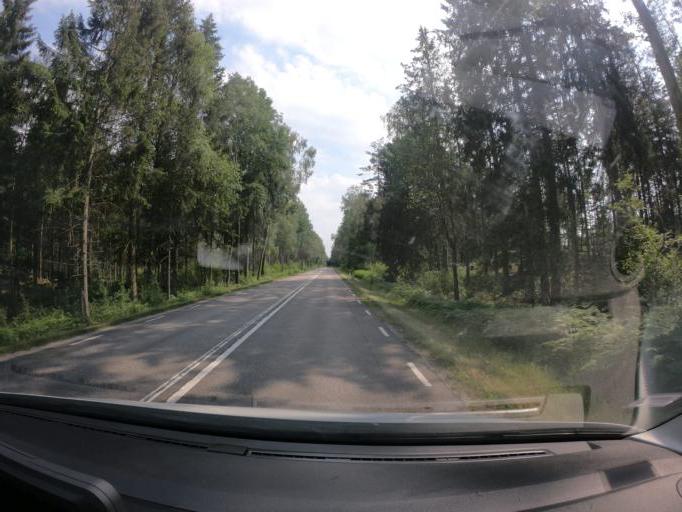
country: SE
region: Skane
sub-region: Hassleholms Kommun
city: Bjarnum
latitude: 56.3583
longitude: 13.6588
